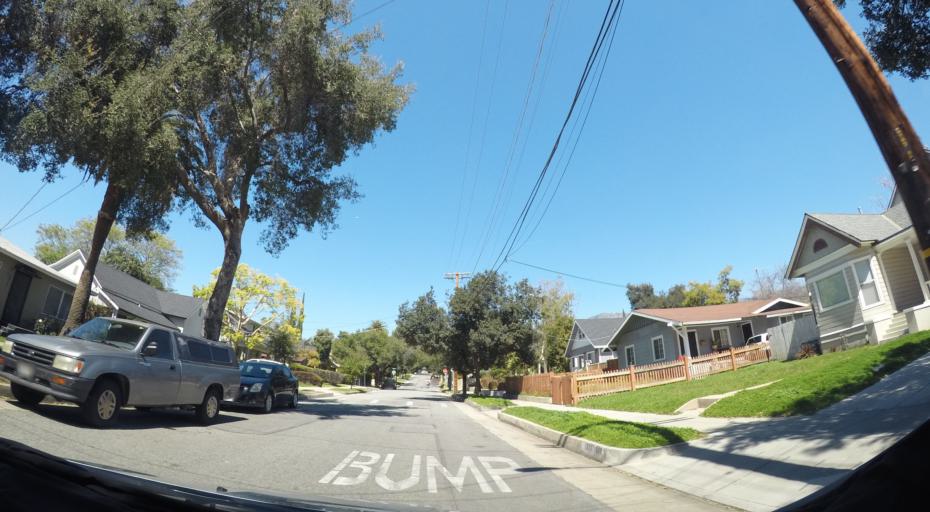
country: US
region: California
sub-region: Los Angeles County
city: Pasadena
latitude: 34.1607
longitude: -118.1438
